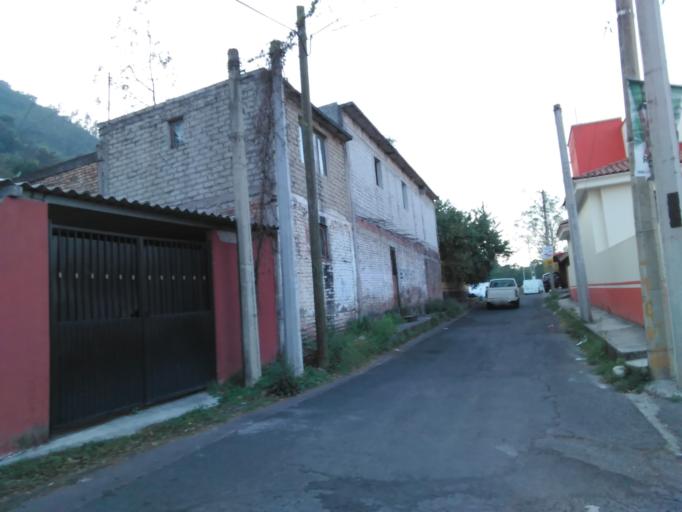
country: MX
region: Nayarit
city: Tepic
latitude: 21.5111
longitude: -104.9228
